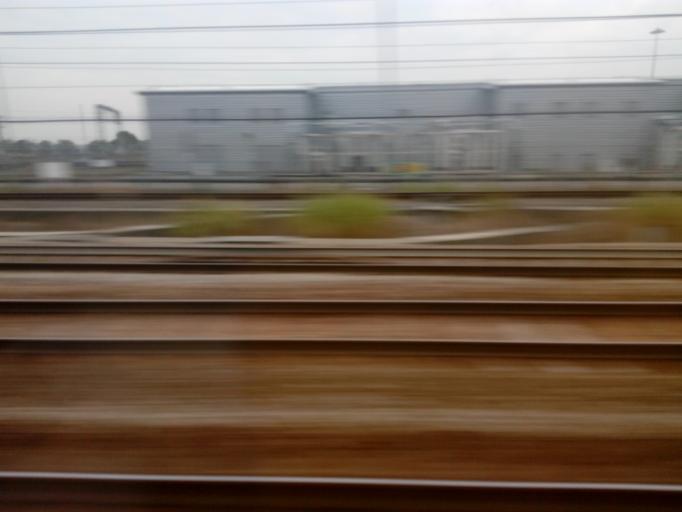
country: HK
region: Tuen Mun
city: Tuen Mun
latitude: 22.3045
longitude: 113.9796
